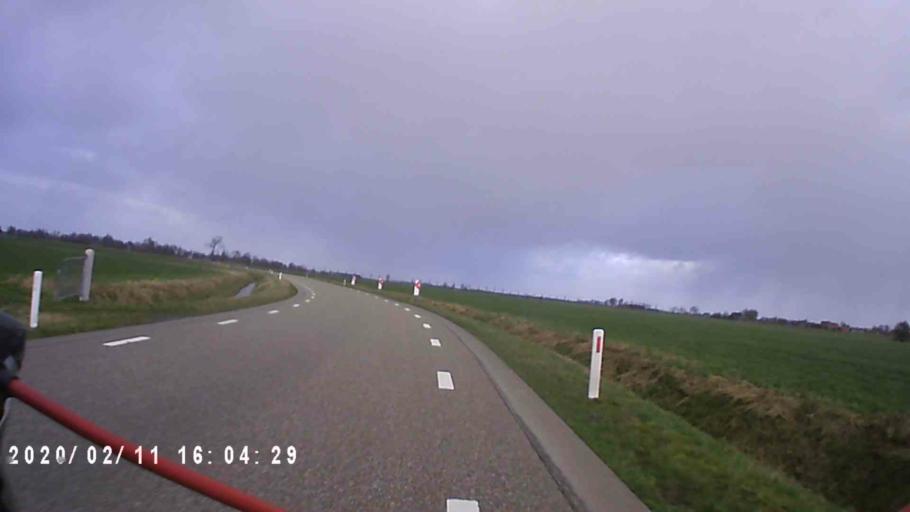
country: NL
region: Groningen
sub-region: Gemeente Zuidhorn
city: Oldehove
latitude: 53.3052
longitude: 6.4209
